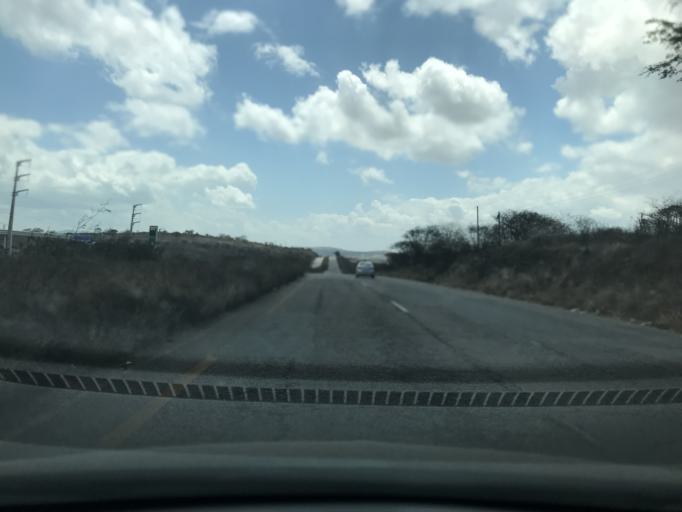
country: BR
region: Pernambuco
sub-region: Caruaru
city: Caruaru
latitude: -8.3049
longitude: -35.9315
